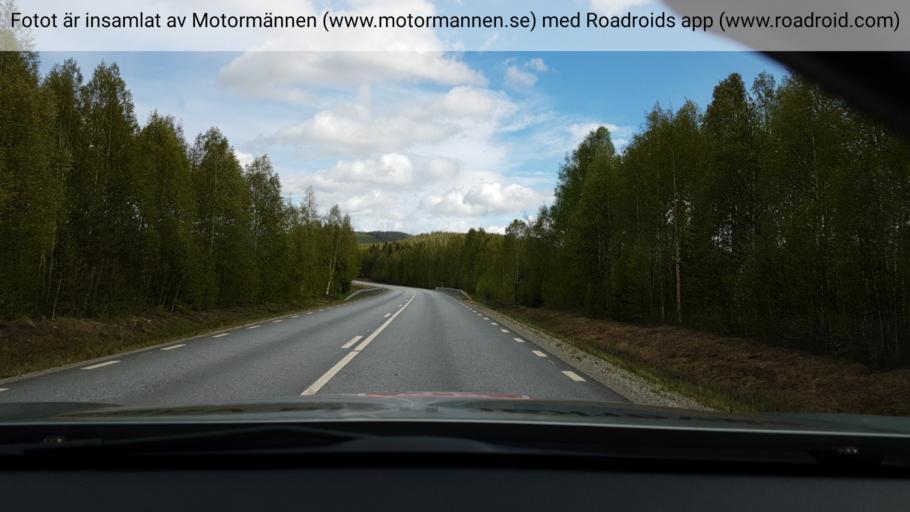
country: SE
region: Vaesterbotten
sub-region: Asele Kommun
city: Insjon
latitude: 64.1962
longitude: 17.6707
